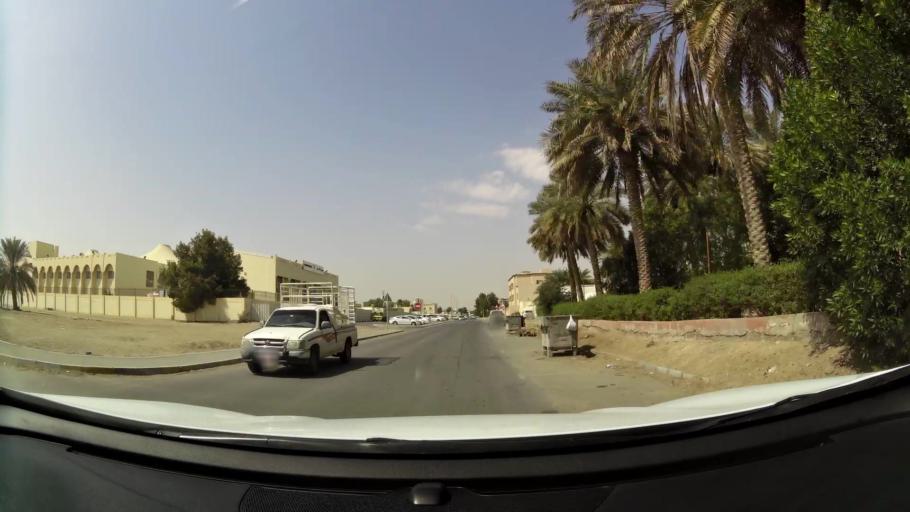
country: AE
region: Abu Dhabi
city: Abu Dhabi
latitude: 24.2856
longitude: 54.6477
